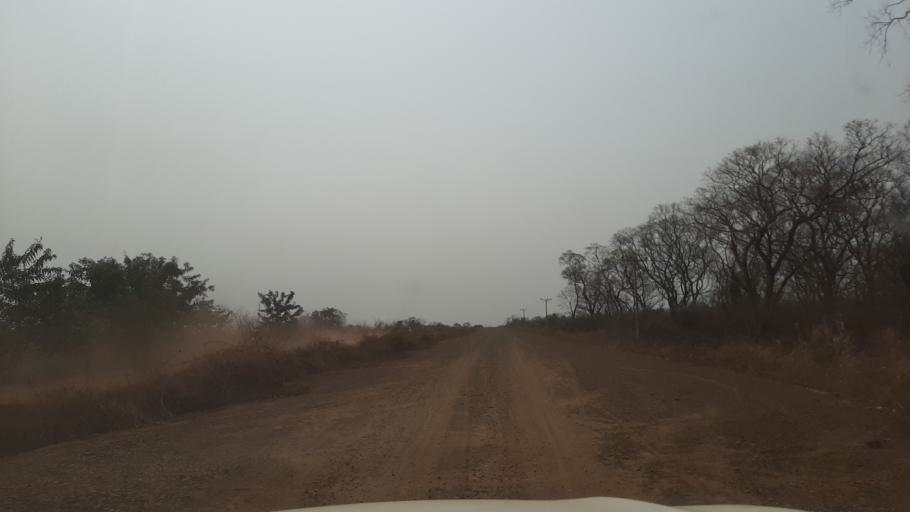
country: ET
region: Gambela
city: Gambela
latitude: 8.1550
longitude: 34.4574
